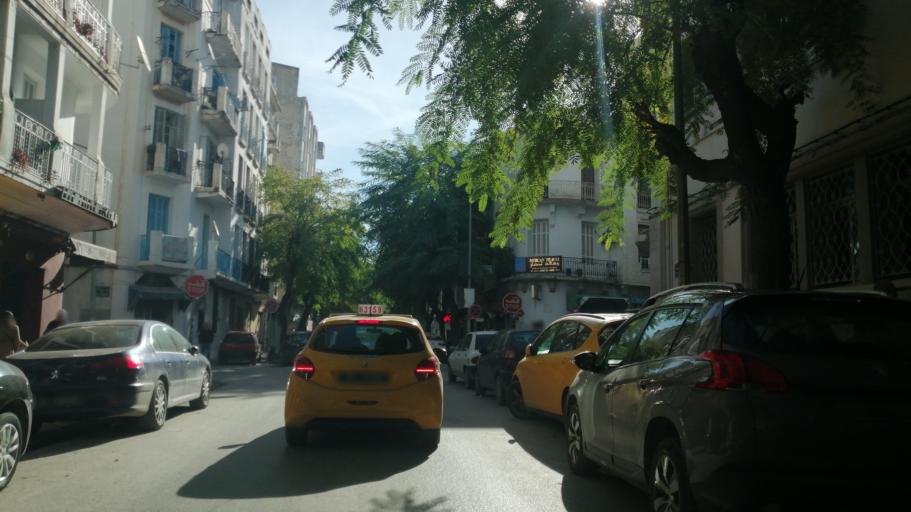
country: TN
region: Tunis
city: Tunis
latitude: 36.8074
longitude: 10.1785
